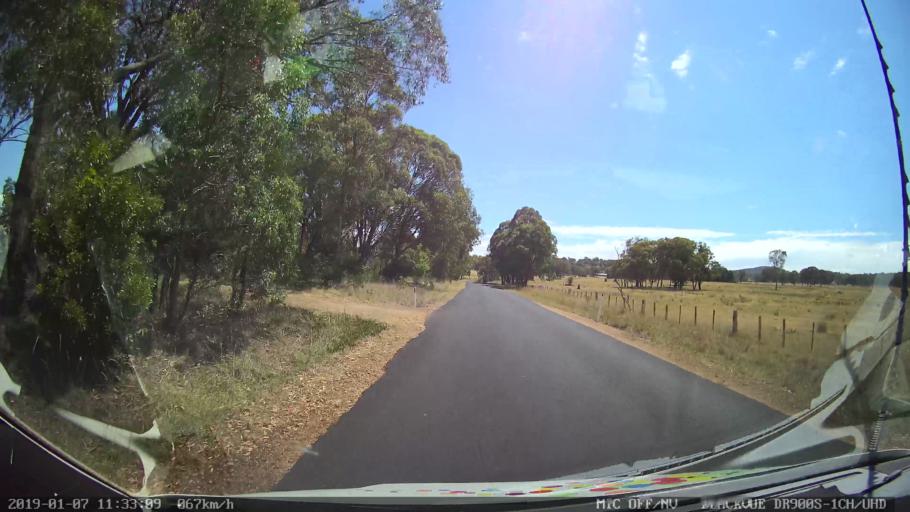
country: AU
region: New South Wales
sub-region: Armidale Dumaresq
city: Armidale
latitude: -30.4030
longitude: 151.5603
